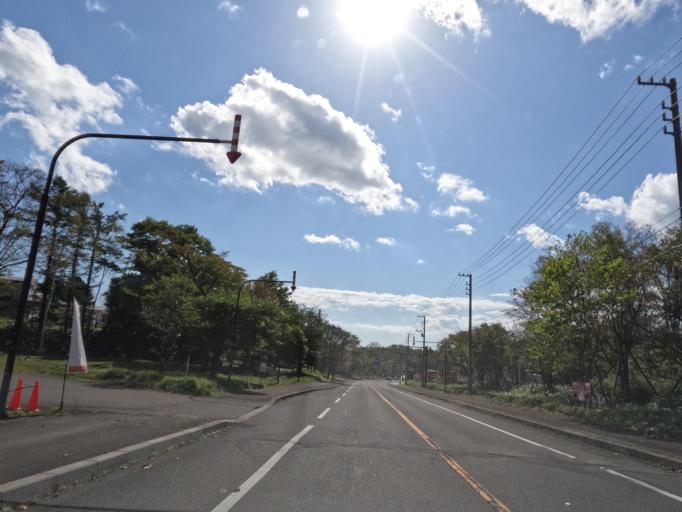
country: JP
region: Hokkaido
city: Shiraoi
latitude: 42.4757
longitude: 141.1473
